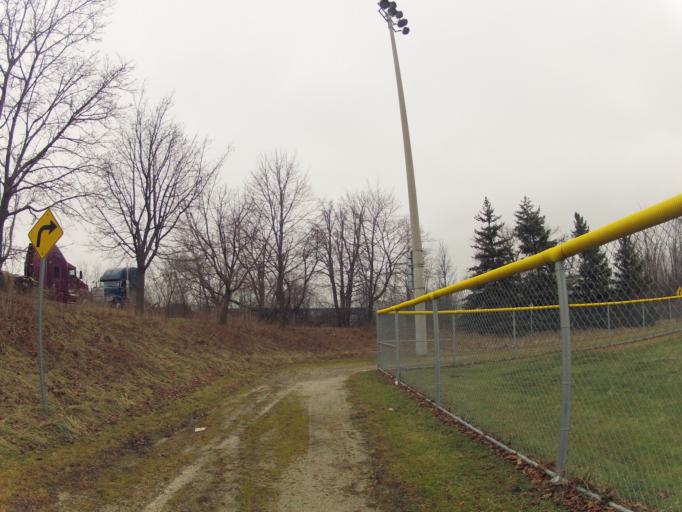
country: CA
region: Ontario
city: Brampton
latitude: 43.6752
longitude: -79.6835
